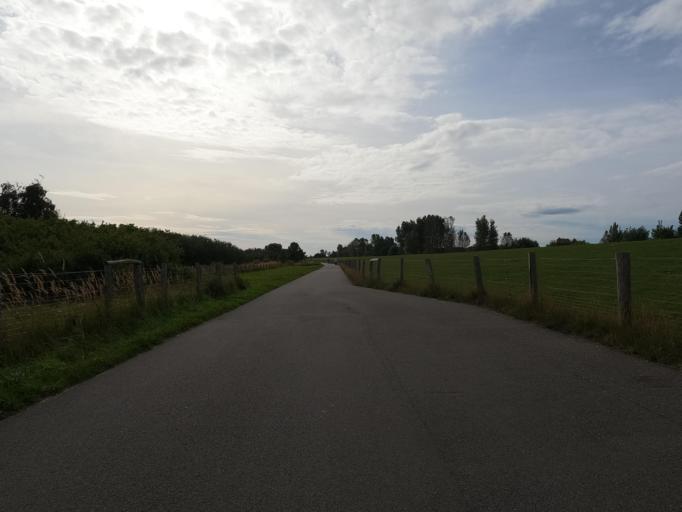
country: DE
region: Schleswig-Holstein
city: Dahme
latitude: 54.2425
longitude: 11.0811
